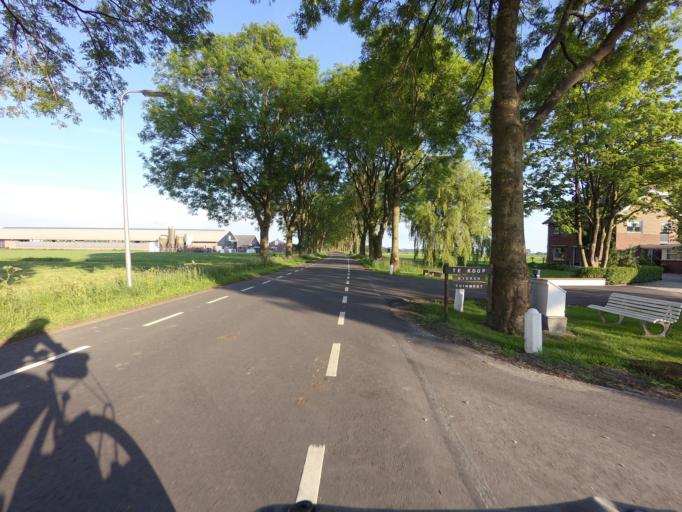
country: NL
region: South Holland
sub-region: Bodegraven-Reeuwijk
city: Bodegraven
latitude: 52.0867
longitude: 4.7213
